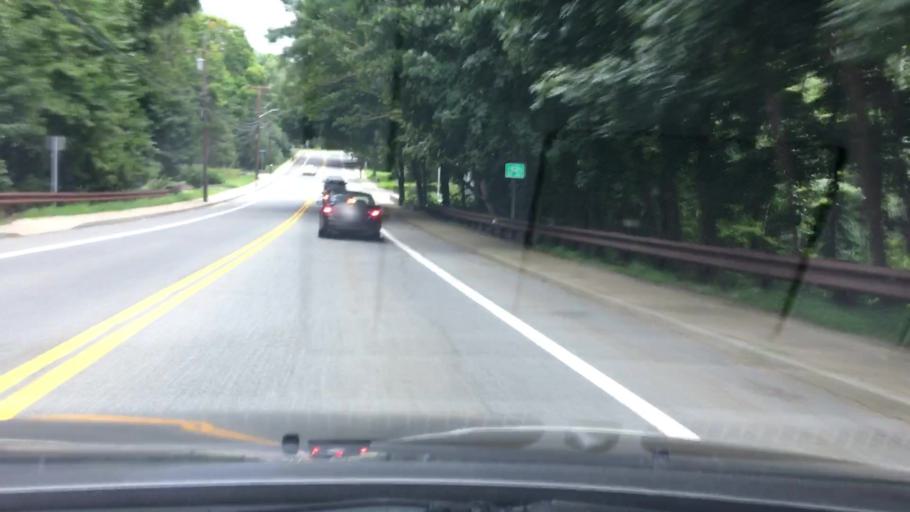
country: US
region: Rhode Island
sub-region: Providence County
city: Cumberland
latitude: 41.9750
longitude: -71.3880
